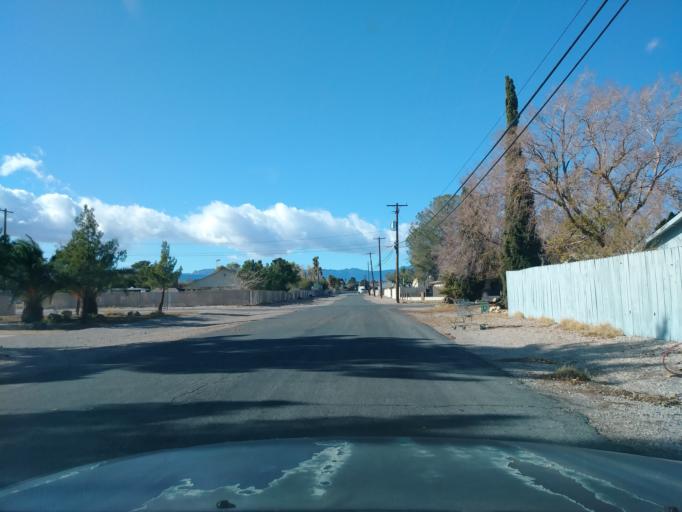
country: US
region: Nevada
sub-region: Clark County
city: Spring Valley
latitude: 36.1500
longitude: -115.2205
